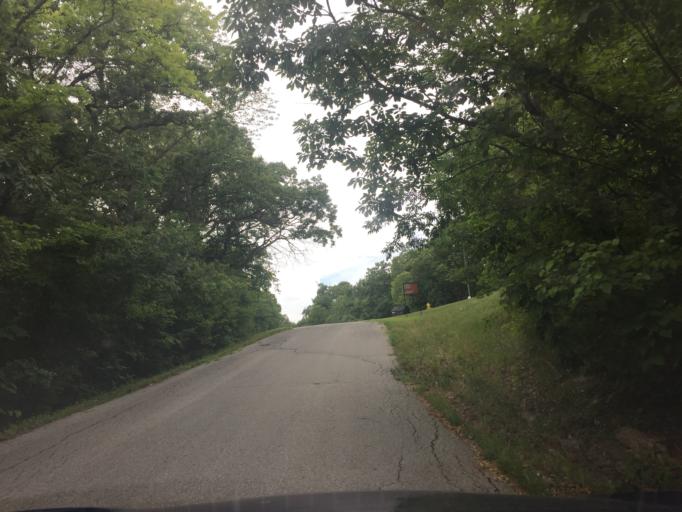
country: US
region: Missouri
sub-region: Platte County
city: Weston
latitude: 39.3711
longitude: -94.9324
